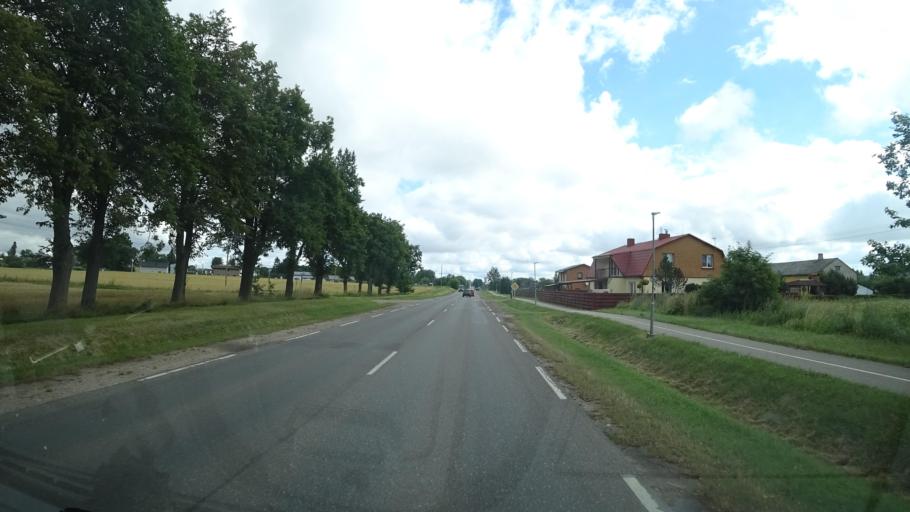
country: LT
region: Marijampoles apskritis
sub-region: Marijampole Municipality
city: Marijampole
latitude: 54.5309
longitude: 23.3313
